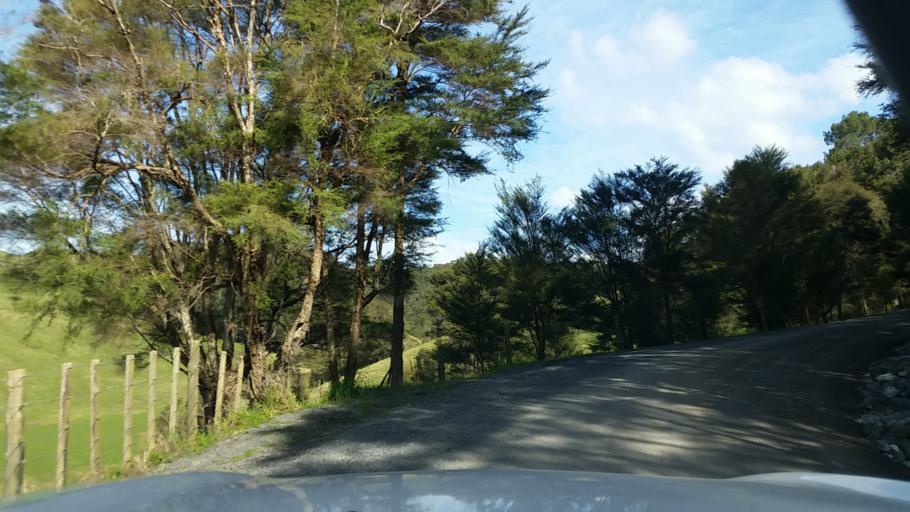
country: NZ
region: Waikato
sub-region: Hauraki District
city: Ngatea
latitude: -37.4469
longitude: 175.4851
